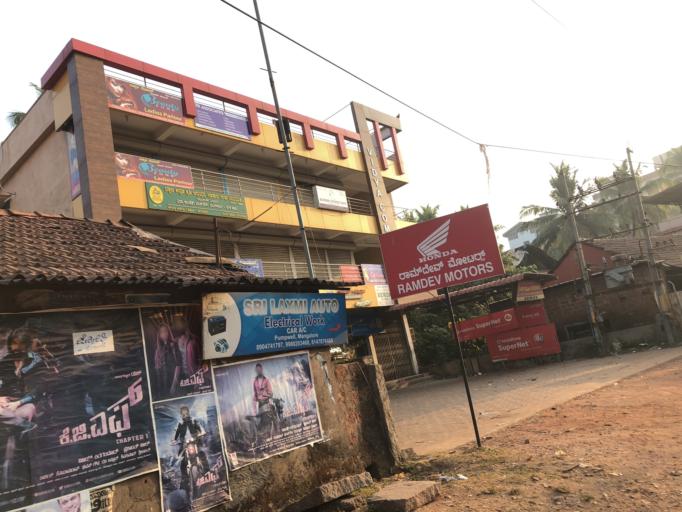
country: IN
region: Karnataka
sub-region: Dakshina Kannada
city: Mangalore
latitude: 12.8698
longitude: 74.8665
